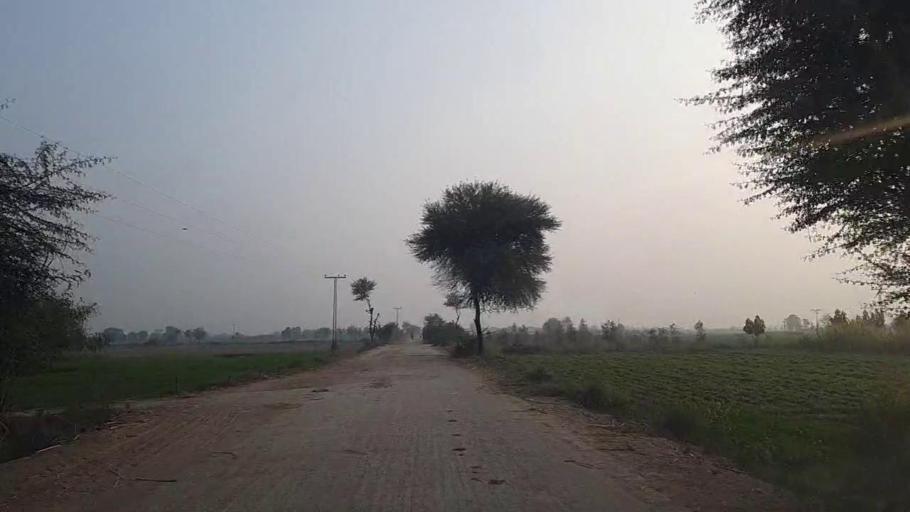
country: PK
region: Sindh
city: Sinjhoro
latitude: 26.1118
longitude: 68.7964
